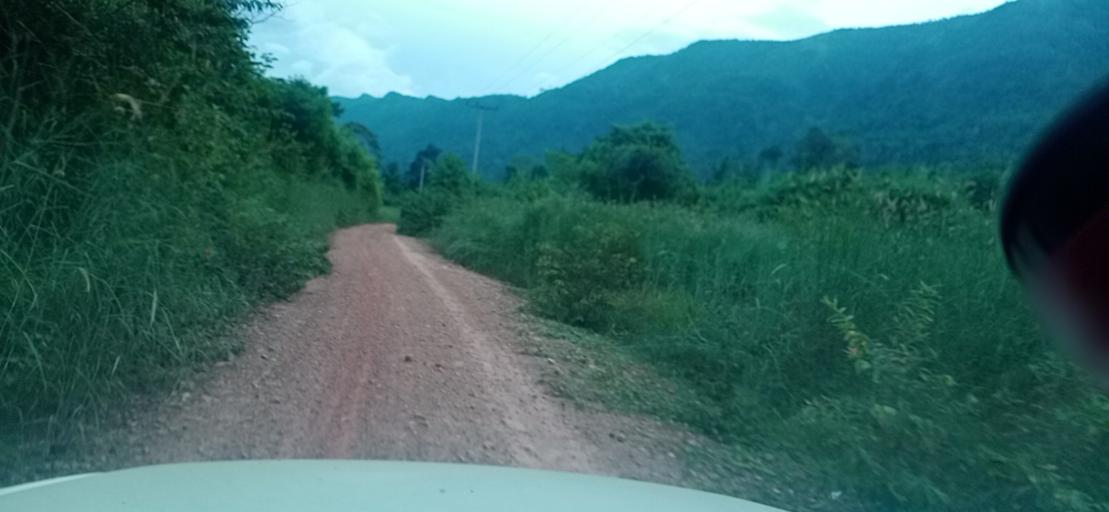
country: TH
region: Changwat Bueng Kan
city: Pak Khat
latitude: 18.5628
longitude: 103.2847
